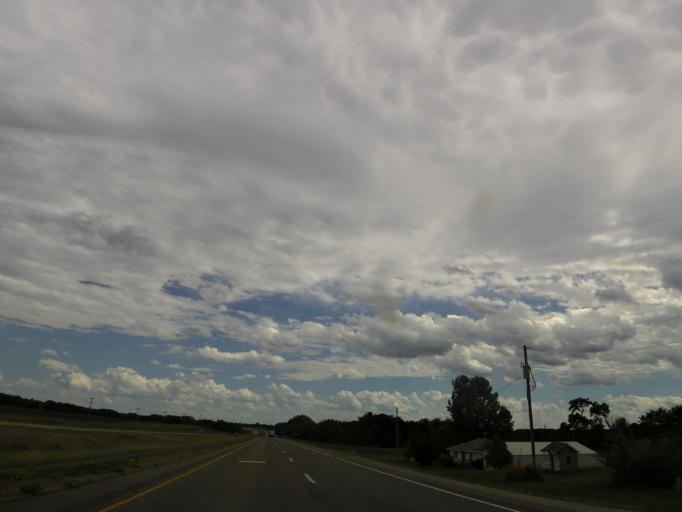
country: US
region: Iowa
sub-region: Henry County
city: Mount Pleasant
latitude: 41.0166
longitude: -91.5491
